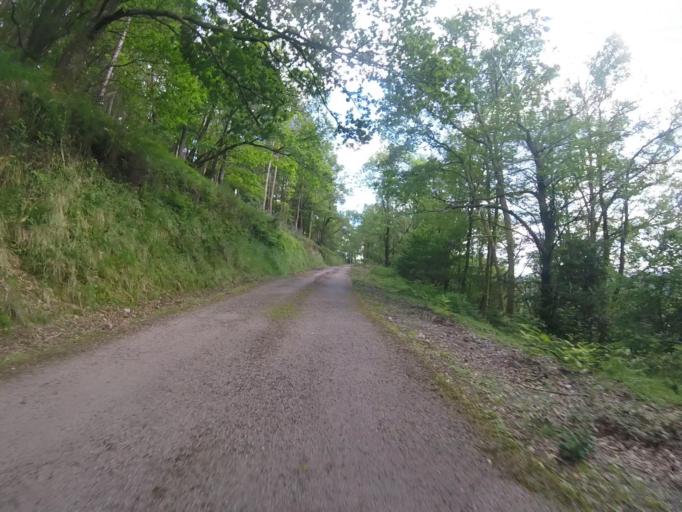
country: ES
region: Navarre
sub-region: Provincia de Navarra
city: Goizueta
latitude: 43.2214
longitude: -1.8033
